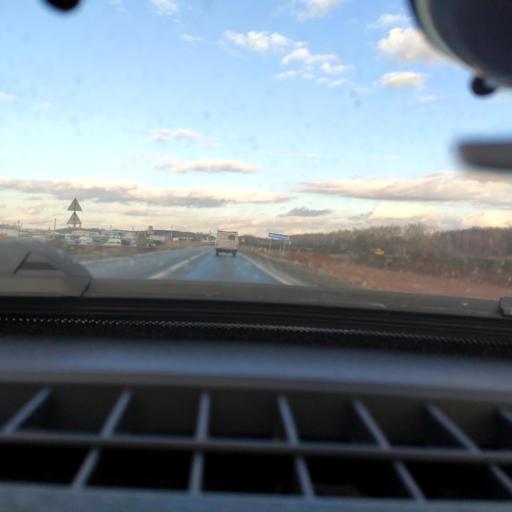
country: RU
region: Bashkortostan
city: Iglino
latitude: 54.7354
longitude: 56.2777
